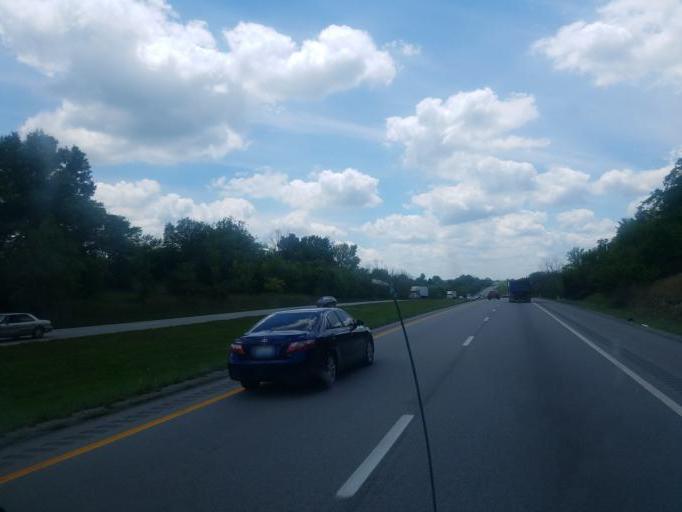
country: US
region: Kentucky
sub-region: Trimble County
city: Providence
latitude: 38.5336
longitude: -85.2224
